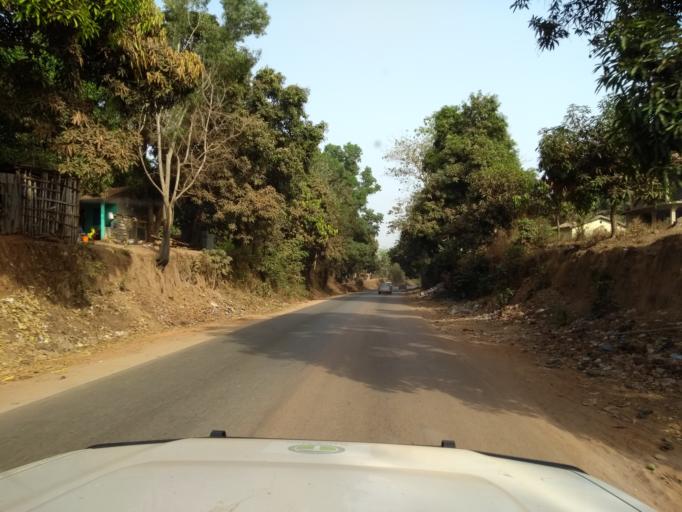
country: GN
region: Kindia
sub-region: Prefecture de Dubreka
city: Dubreka
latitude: 9.8363
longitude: -13.4864
